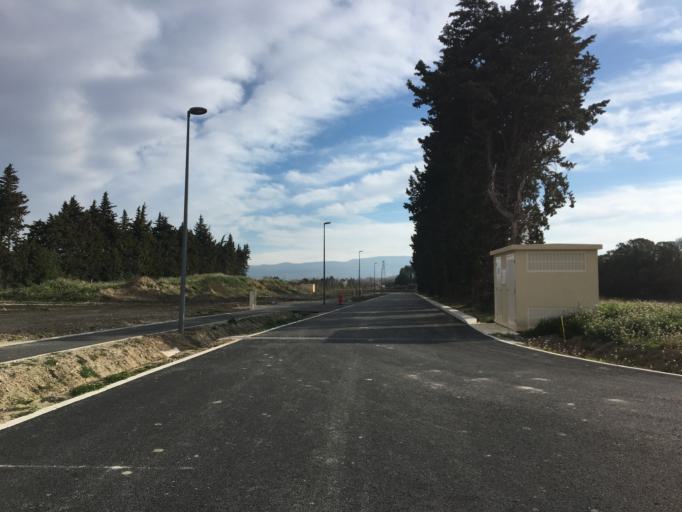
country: FR
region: Provence-Alpes-Cote d'Azur
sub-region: Departement du Vaucluse
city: Le Thor
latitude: 43.9270
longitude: 5.0147
